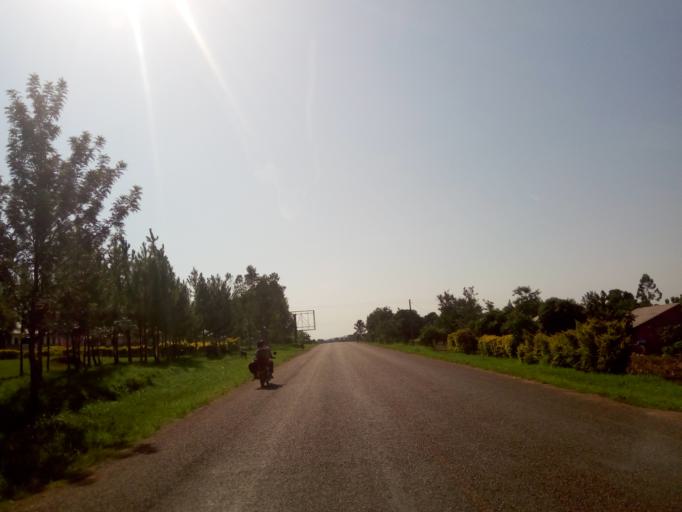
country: UG
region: Western Region
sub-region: Masindi District
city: Masindi
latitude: 1.6729
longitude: 31.7395
